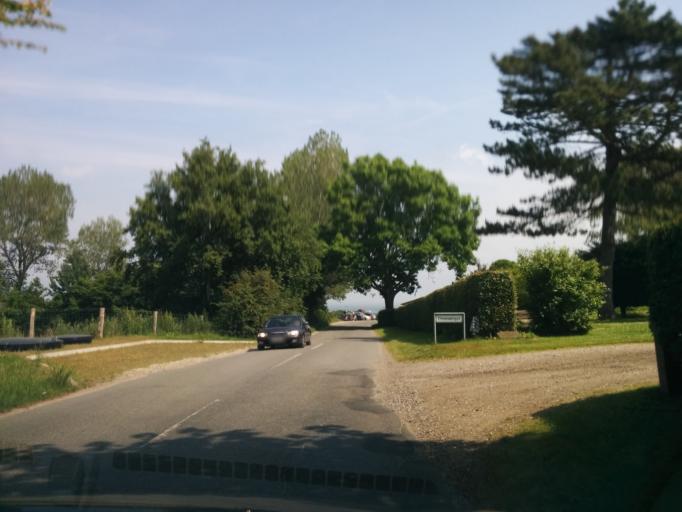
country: DK
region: Central Jutland
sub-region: Arhus Kommune
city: Beder
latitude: 56.0403
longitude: 10.2684
